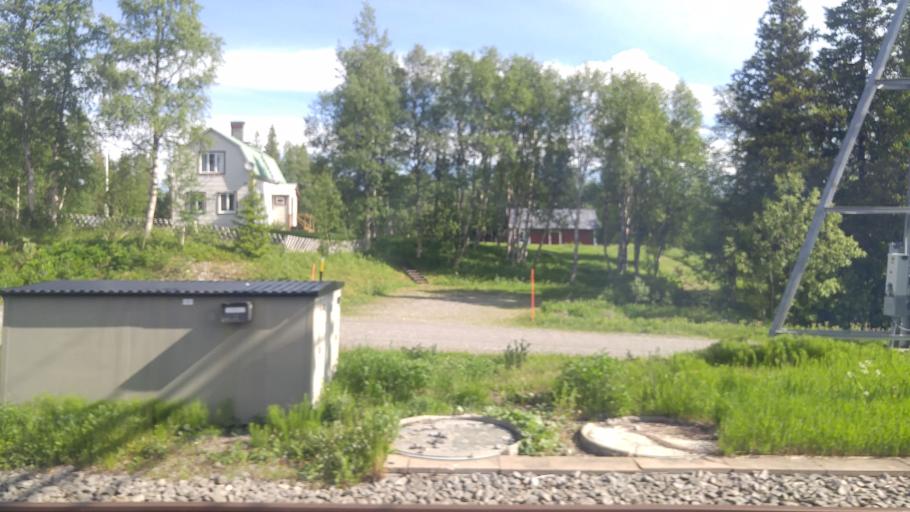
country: NO
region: Nord-Trondelag
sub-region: Meraker
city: Meraker
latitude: 63.2896
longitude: 12.3385
